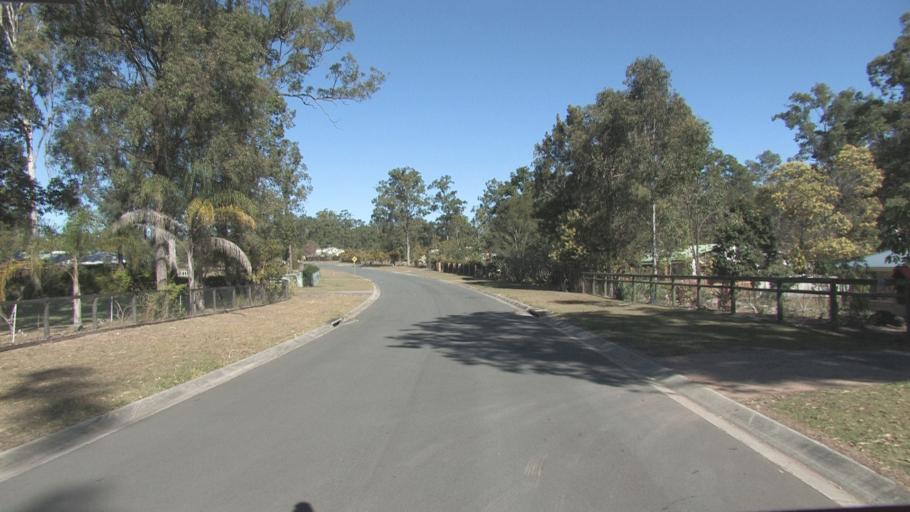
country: AU
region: Queensland
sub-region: Logan
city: North Maclean
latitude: -27.8224
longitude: 152.9435
